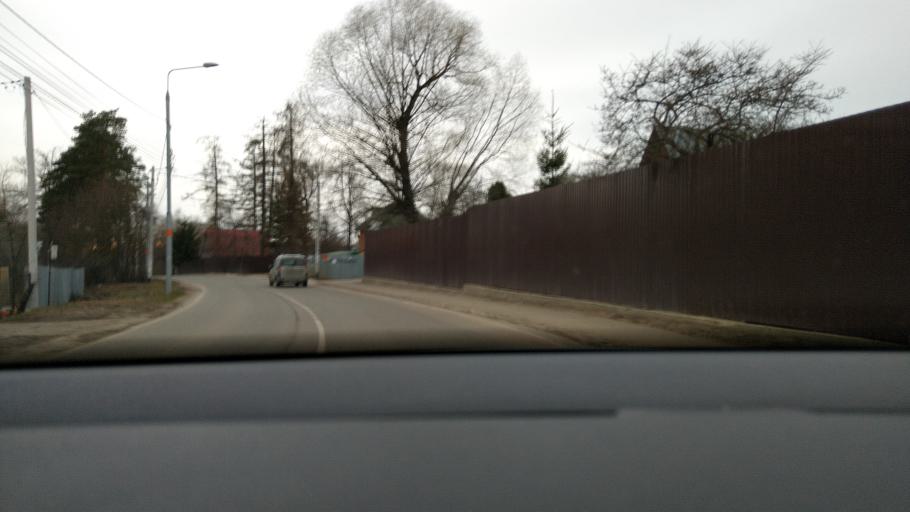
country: RU
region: Moskovskaya
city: Mosrentgen
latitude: 55.5930
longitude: 37.4484
